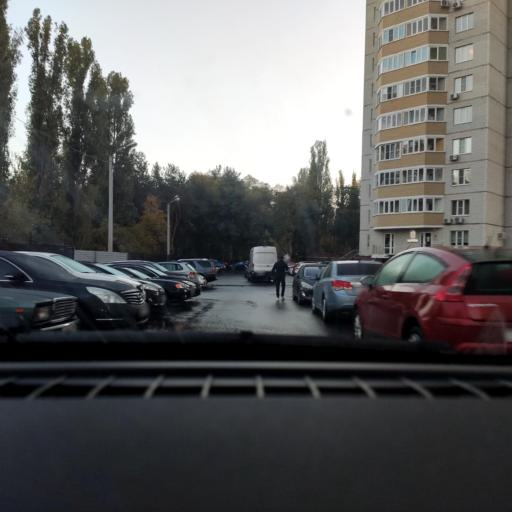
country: RU
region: Voronezj
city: Voronezh
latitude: 51.6842
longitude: 39.2529
